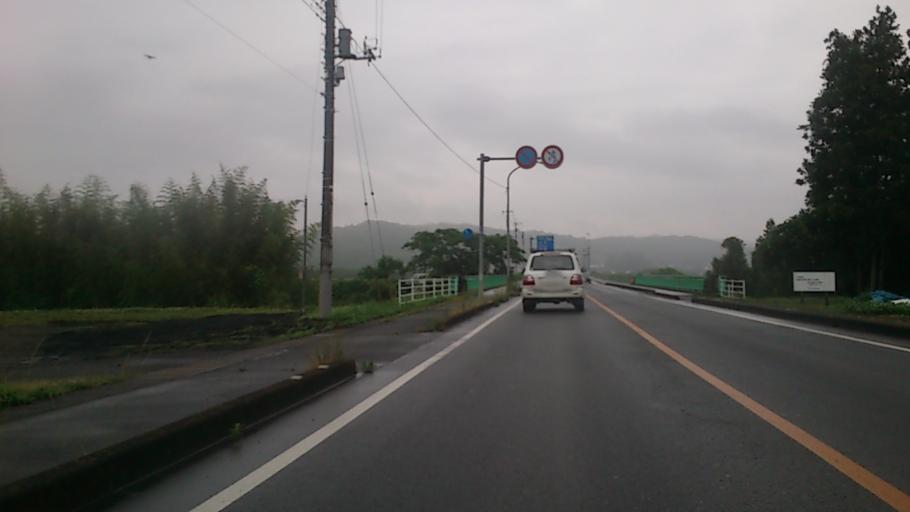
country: JP
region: Tochigi
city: Karasuyama
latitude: 36.7511
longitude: 140.1337
